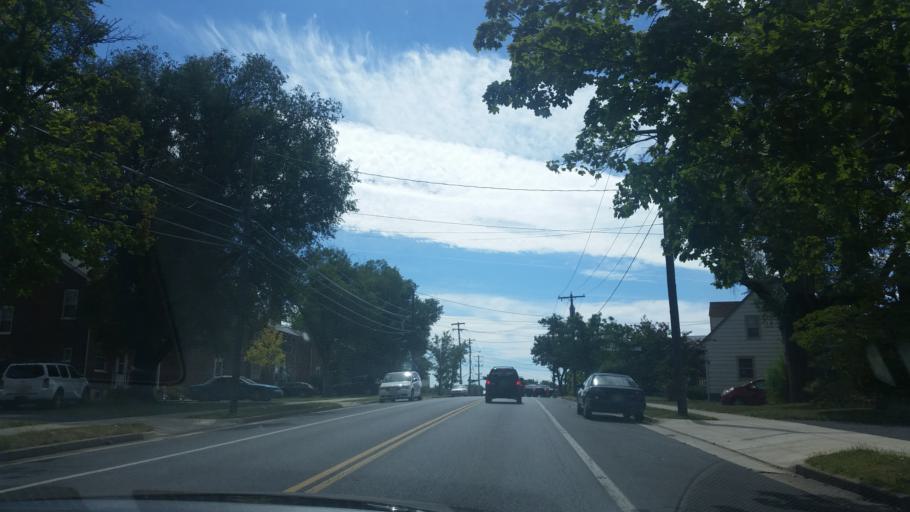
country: US
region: Virginia
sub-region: City of Winchester
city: Winchester
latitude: 39.1700
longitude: -78.1635
